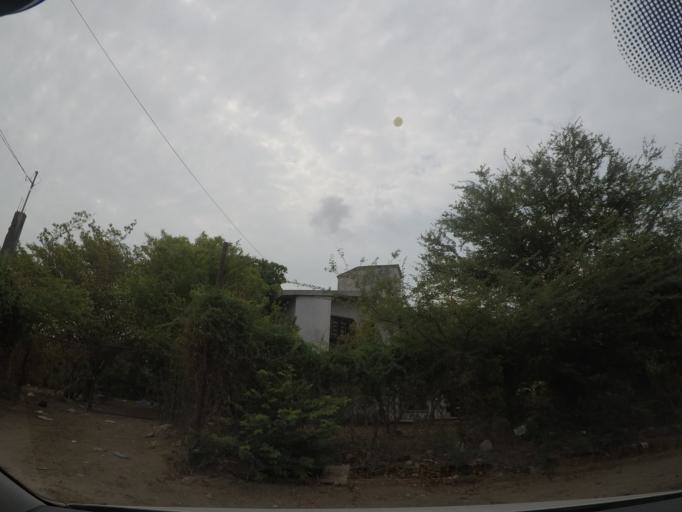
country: MX
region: Oaxaca
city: Juchitan de Zaragoza
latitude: 16.4530
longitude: -95.0144
